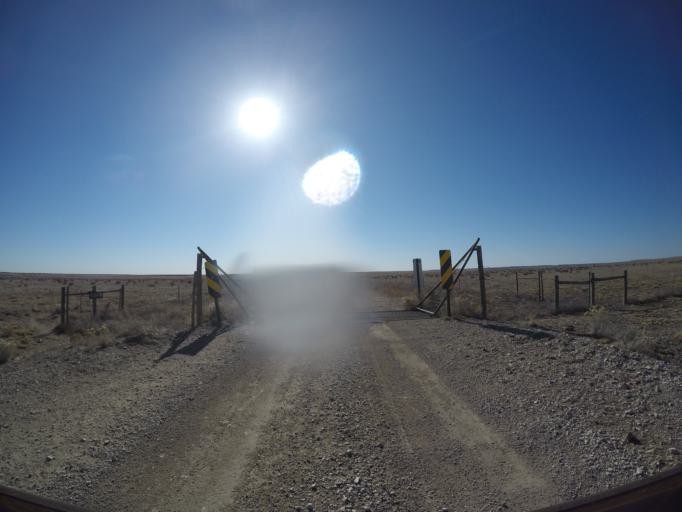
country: US
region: Colorado
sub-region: Otero County
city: La Junta
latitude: 37.7098
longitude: -103.6205
